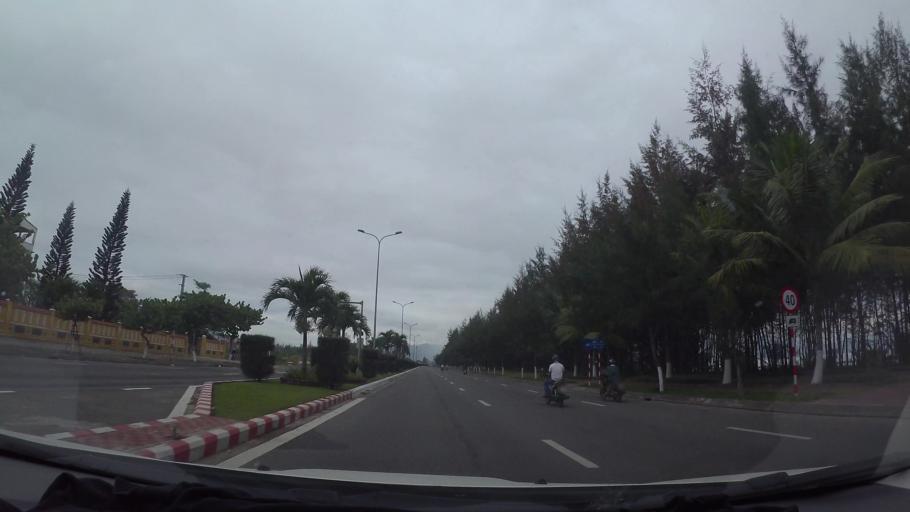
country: VN
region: Da Nang
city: Lien Chieu
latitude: 16.0923
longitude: 108.1493
